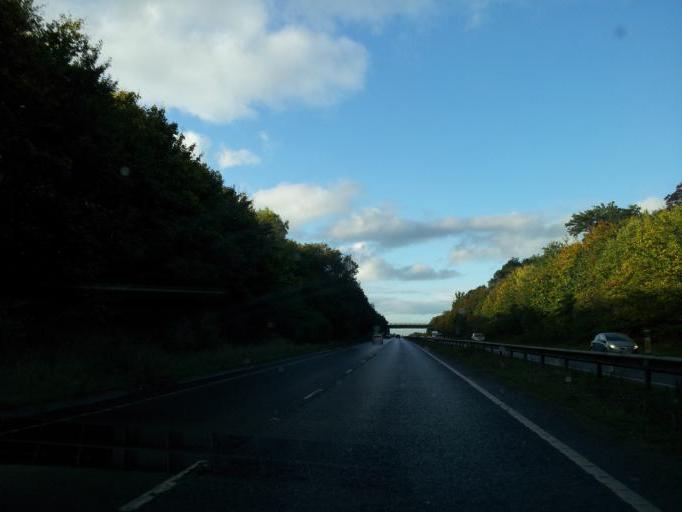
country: GB
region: England
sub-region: Norfolk
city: Thorpe Hamlet
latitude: 52.6132
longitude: 1.3336
